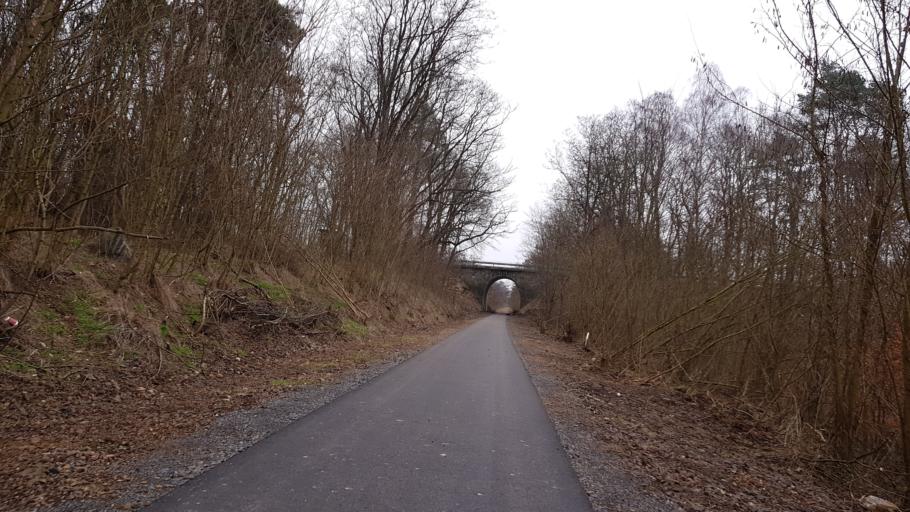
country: PL
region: West Pomeranian Voivodeship
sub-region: Powiat mysliborski
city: Barlinek
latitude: 53.0135
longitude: 15.2626
